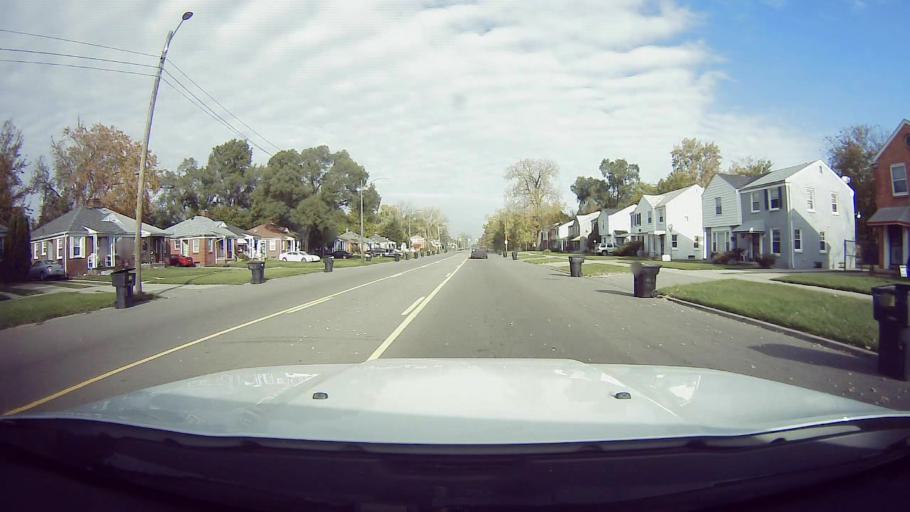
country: US
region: Michigan
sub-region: Oakland County
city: Oak Park
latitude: 42.4367
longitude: -83.1806
